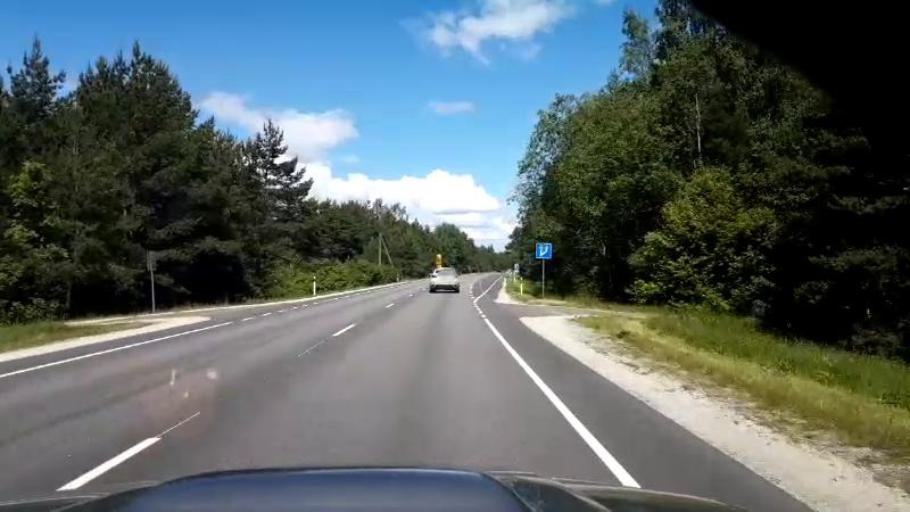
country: EE
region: Paernumaa
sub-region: Paernu linn
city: Parnu
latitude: 58.2117
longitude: 24.4857
